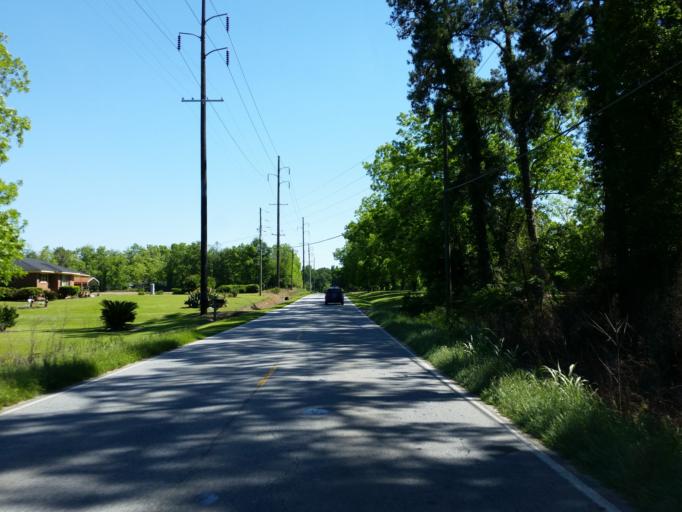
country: US
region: Georgia
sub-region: Lowndes County
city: Hahira
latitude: 30.9281
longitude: -83.3499
